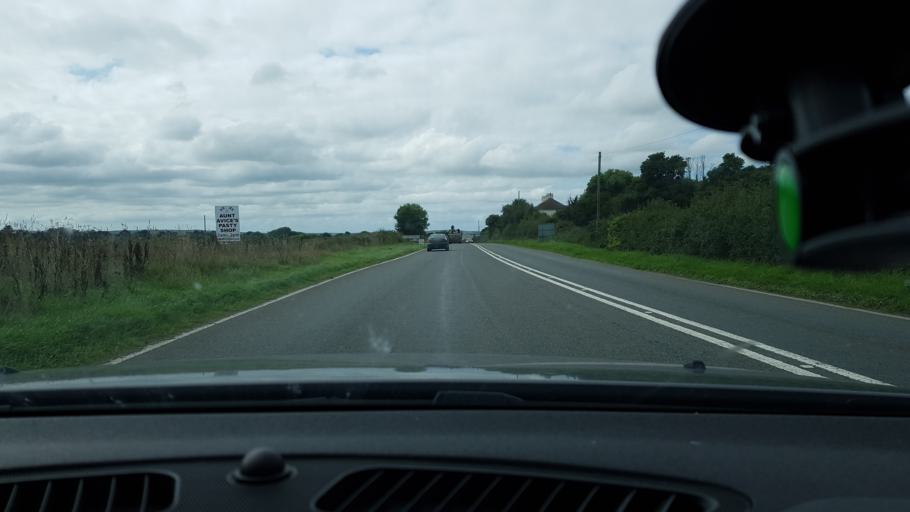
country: GB
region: England
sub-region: Cornwall
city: Helland
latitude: 50.5473
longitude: -4.7708
